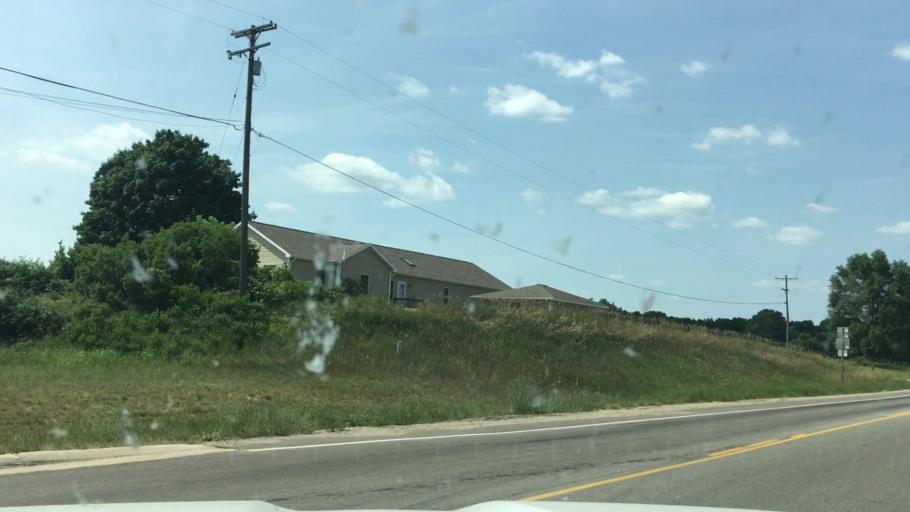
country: US
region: Michigan
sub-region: Allegan County
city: Plainwell
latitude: 42.4432
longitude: -85.6024
